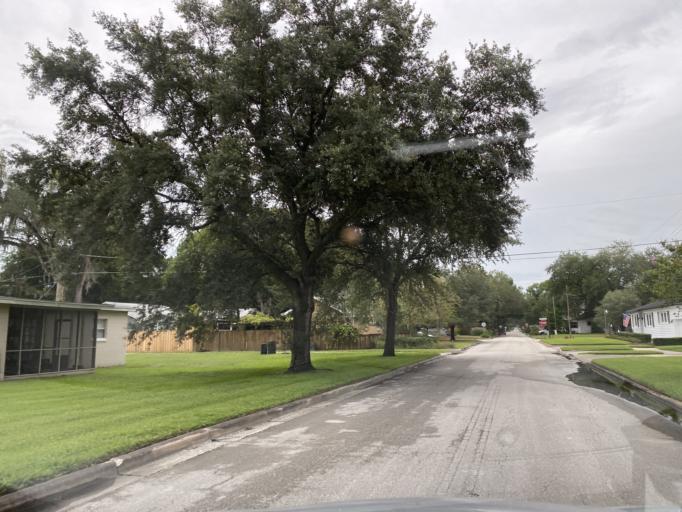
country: US
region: Florida
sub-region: Seminole County
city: Sanford
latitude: 28.8027
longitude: -81.2679
